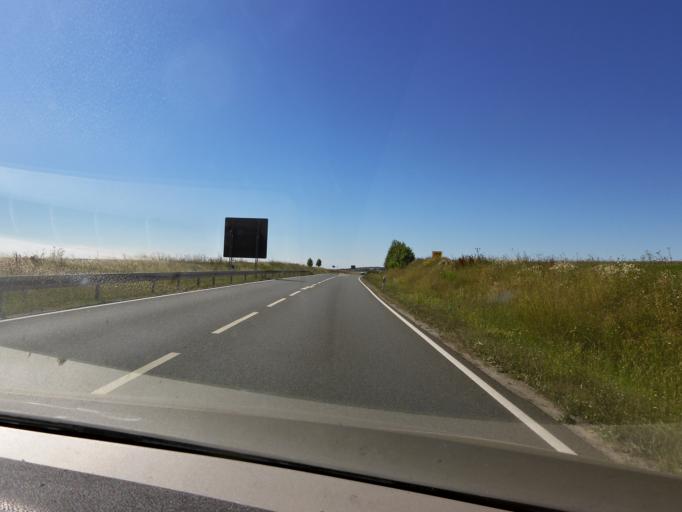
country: DE
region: Bavaria
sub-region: Regierungsbezirk Unterfranken
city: Biebelried
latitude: 49.7619
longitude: 10.0989
